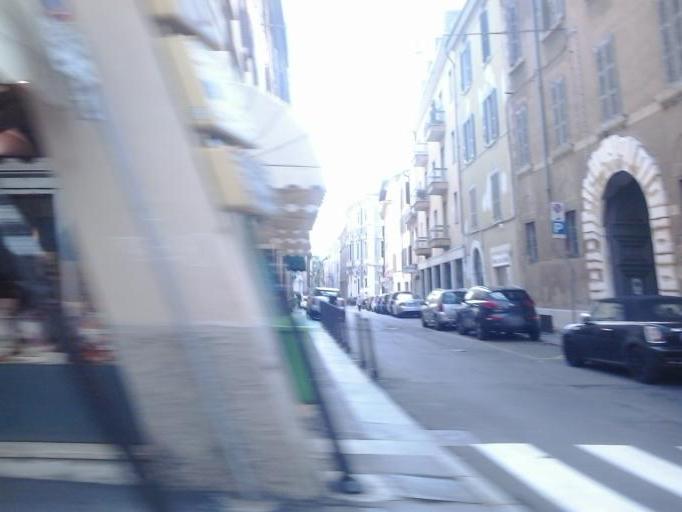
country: IT
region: Lombardy
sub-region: Provincia di Brescia
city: Brescia
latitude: 45.5353
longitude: 10.2216
